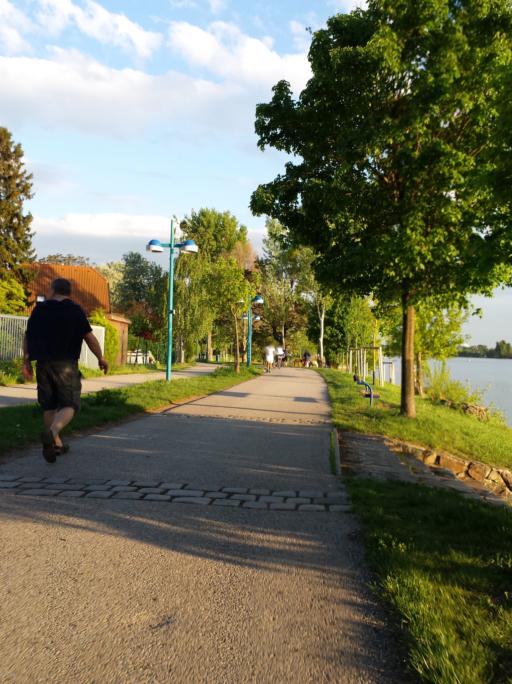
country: AT
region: Vienna
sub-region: Wien Stadt
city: Vienna
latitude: 48.2273
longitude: 16.4359
